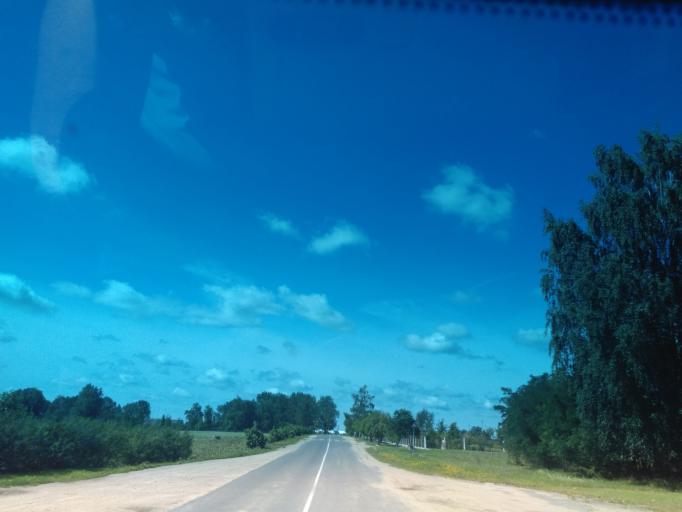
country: BY
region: Minsk
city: Kapyl'
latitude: 53.2592
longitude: 27.1884
